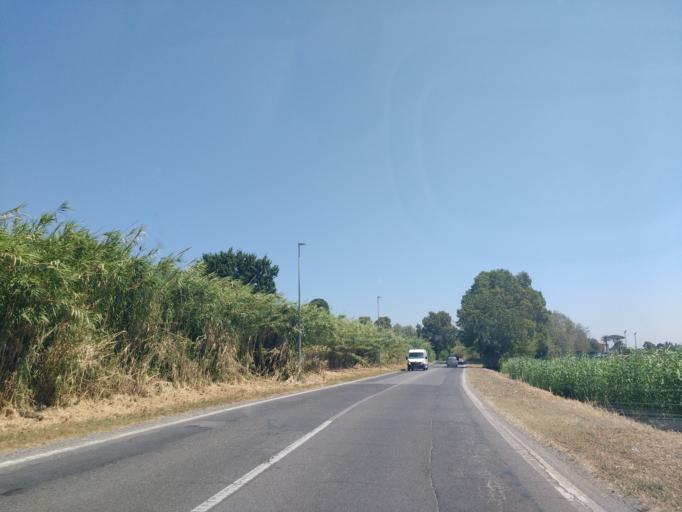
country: IT
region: Latium
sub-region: Citta metropolitana di Roma Capitale
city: Maccarese
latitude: 41.8740
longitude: 12.2099
